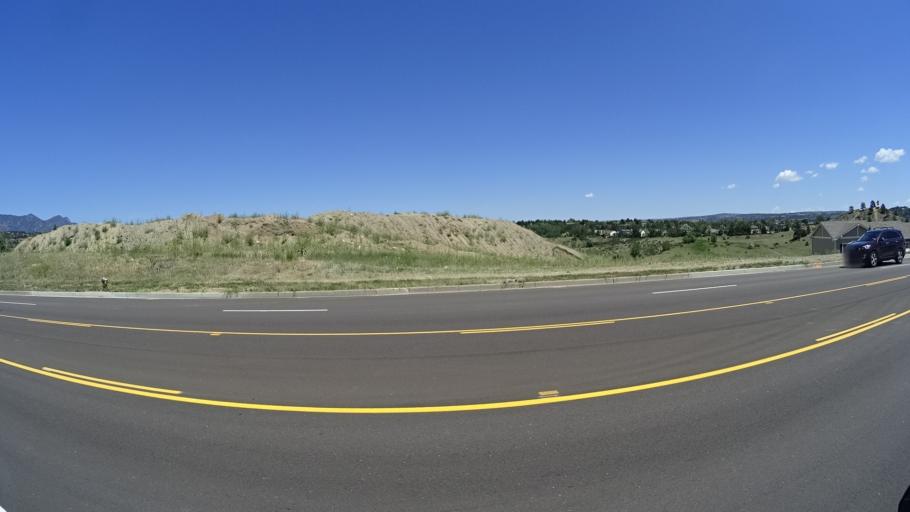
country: US
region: Colorado
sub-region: El Paso County
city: Air Force Academy
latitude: 38.9169
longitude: -104.8325
